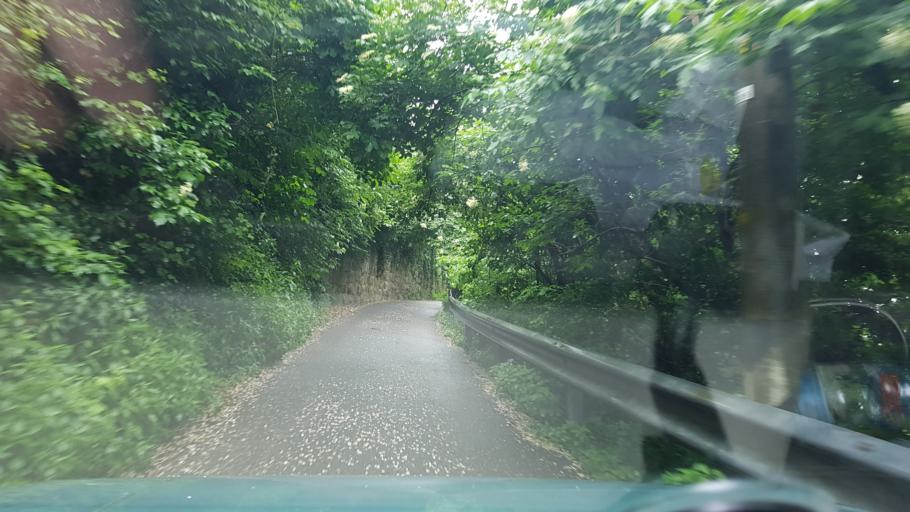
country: IT
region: Friuli Venezia Giulia
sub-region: Provincia di Trieste
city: Villa Opicina
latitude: 45.6731
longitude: 13.7811
